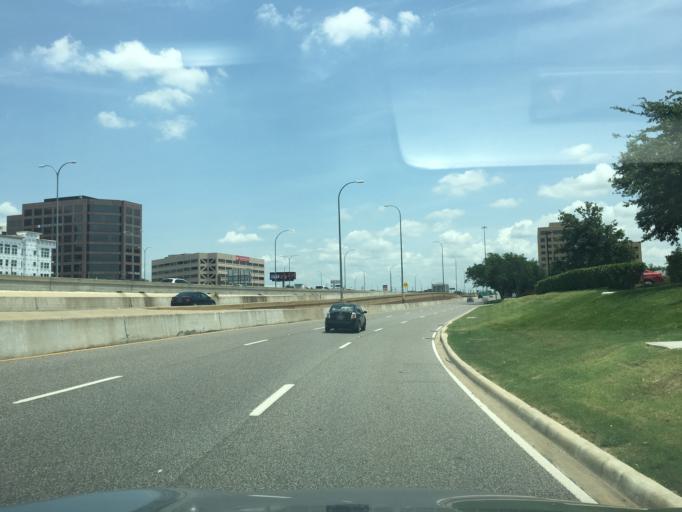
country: US
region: Texas
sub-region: Dallas County
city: Addison
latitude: 32.9253
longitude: -96.8177
